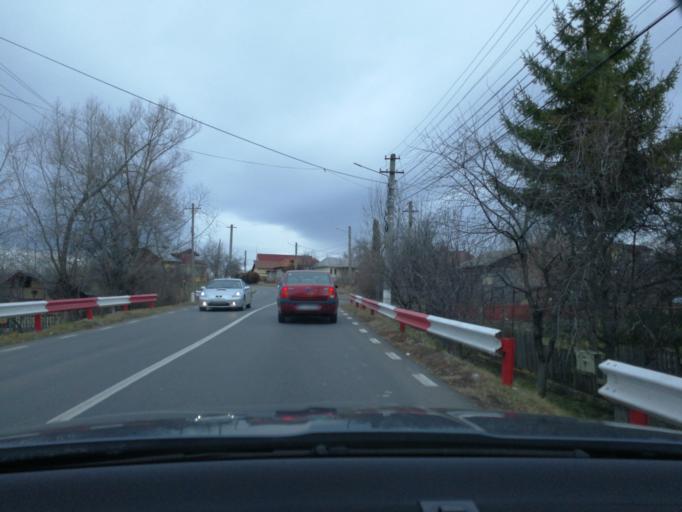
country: RO
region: Prahova
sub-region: Oras Breaza
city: Breaza de Jos
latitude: 45.1610
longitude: 25.6854
